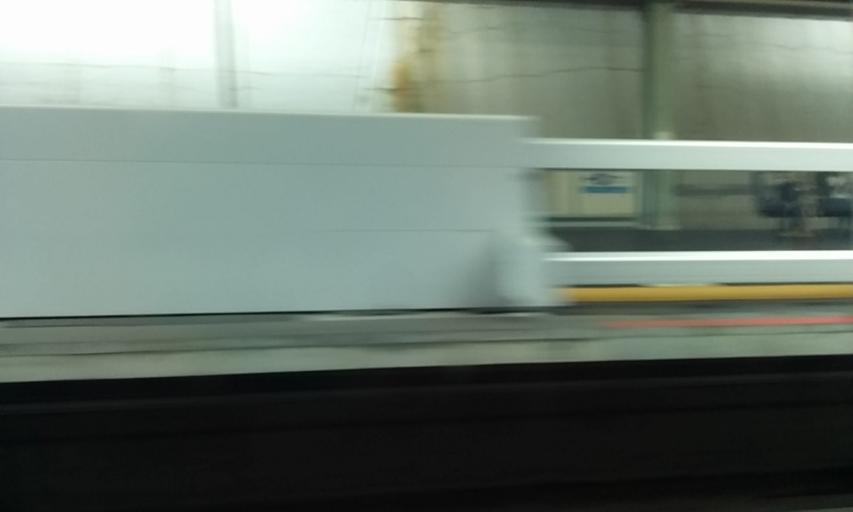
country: JP
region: Hyogo
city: Kobe
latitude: 34.7083
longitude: 135.2002
